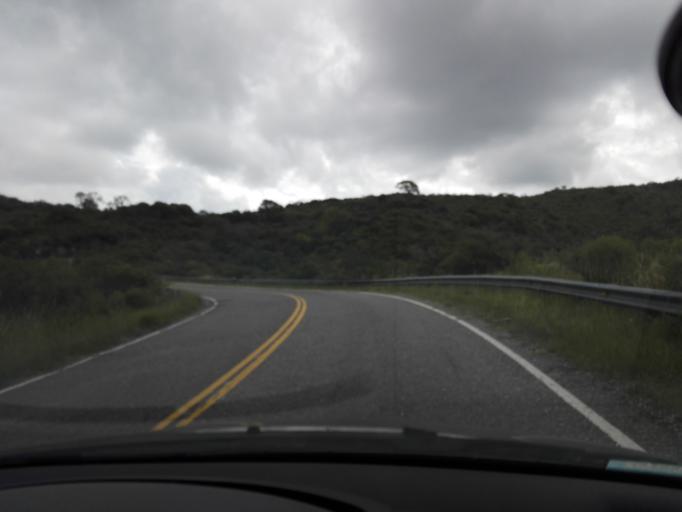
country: AR
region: Cordoba
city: Alta Gracia
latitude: -31.5919
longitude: -64.5184
